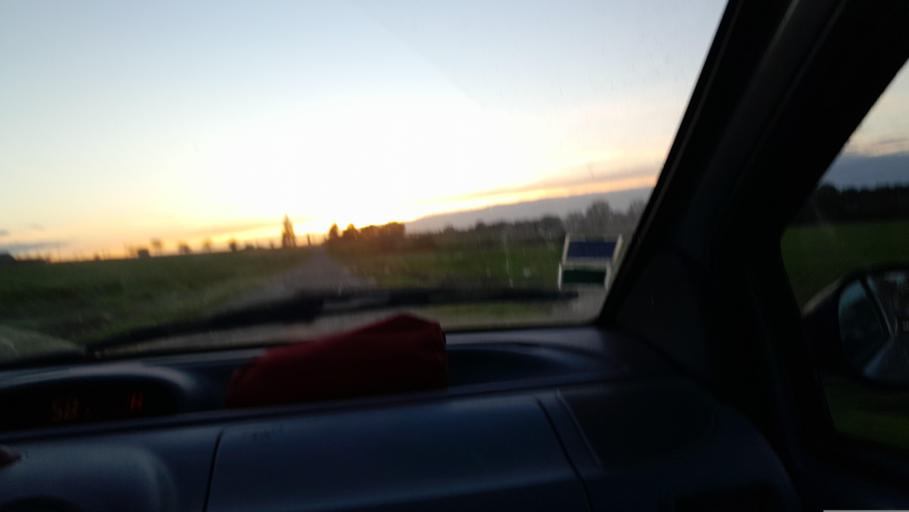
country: FR
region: Brittany
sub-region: Departement d'Ille-et-Vilaine
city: La Guerche-de-Bretagne
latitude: 47.8936
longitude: -1.1637
